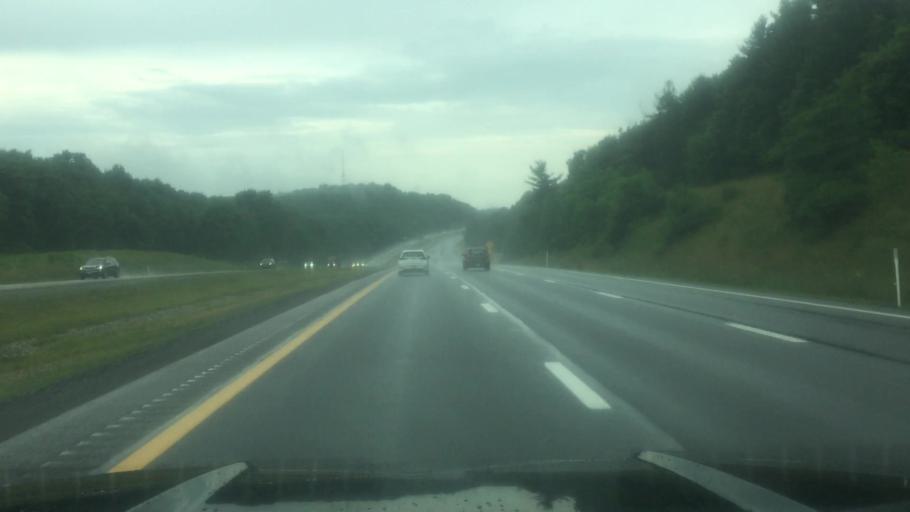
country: US
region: West Virginia
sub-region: Raleigh County
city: Shady Spring
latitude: 37.5841
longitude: -81.1209
